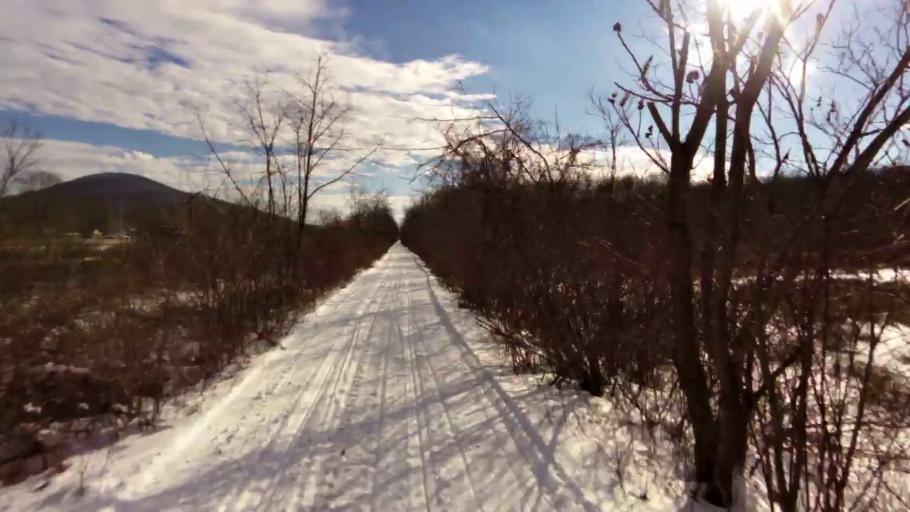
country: US
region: Pennsylvania
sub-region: McKean County
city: Foster Brook
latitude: 42.0326
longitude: -78.6326
